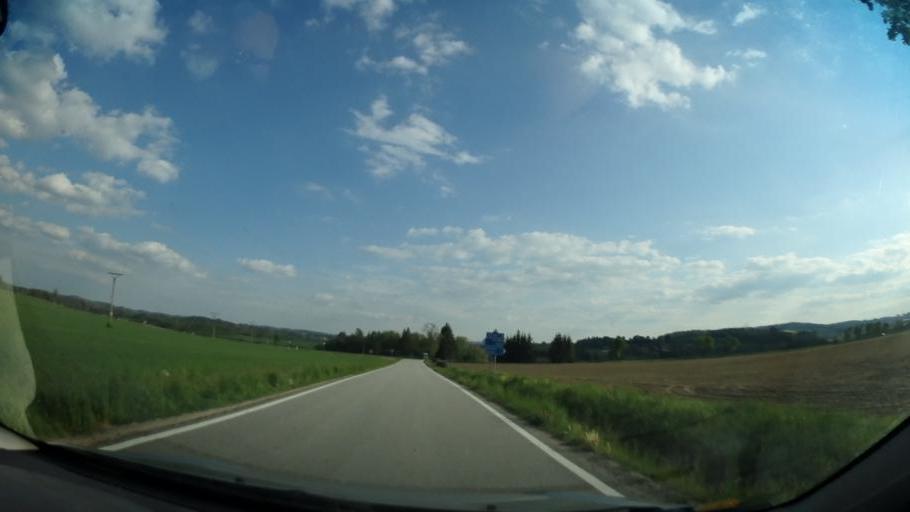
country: CZ
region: Vysocina
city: Merin
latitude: 49.3576
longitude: 15.9052
